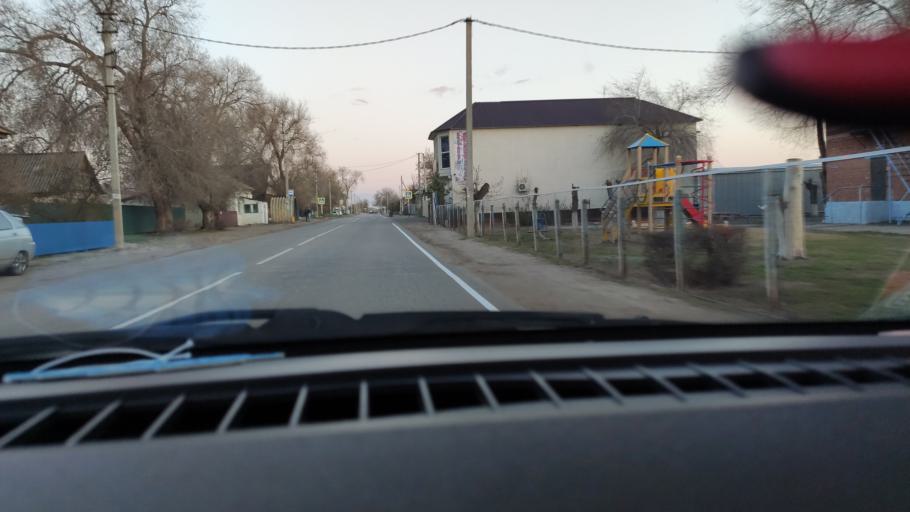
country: RU
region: Saratov
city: Privolzhskiy
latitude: 51.1829
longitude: 45.9188
